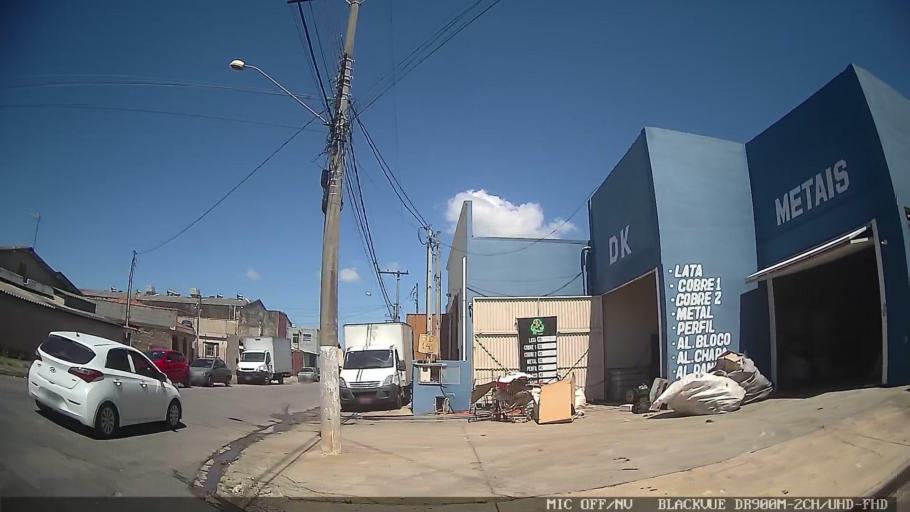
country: BR
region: Sao Paulo
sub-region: Atibaia
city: Atibaia
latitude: -23.1134
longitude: -46.5685
